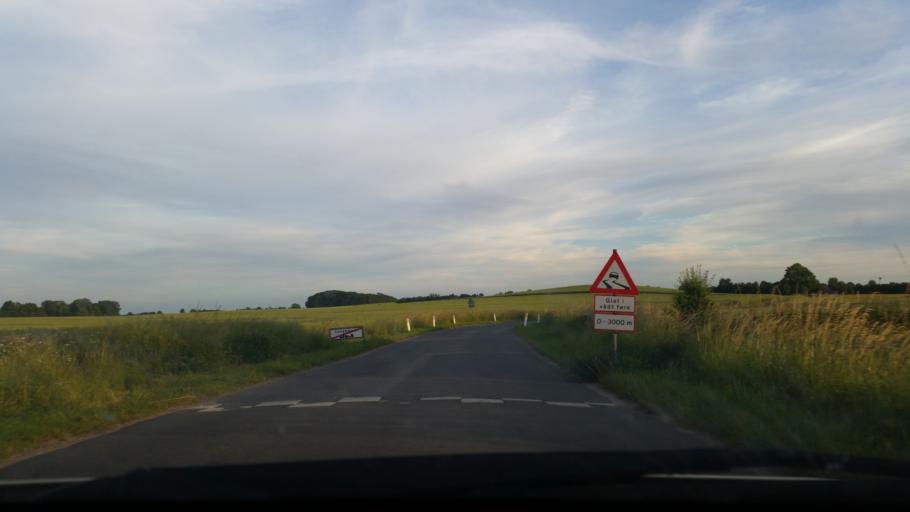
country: DK
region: Central Jutland
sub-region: Samso Kommune
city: Tranebjerg
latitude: 55.8448
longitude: 10.6212
